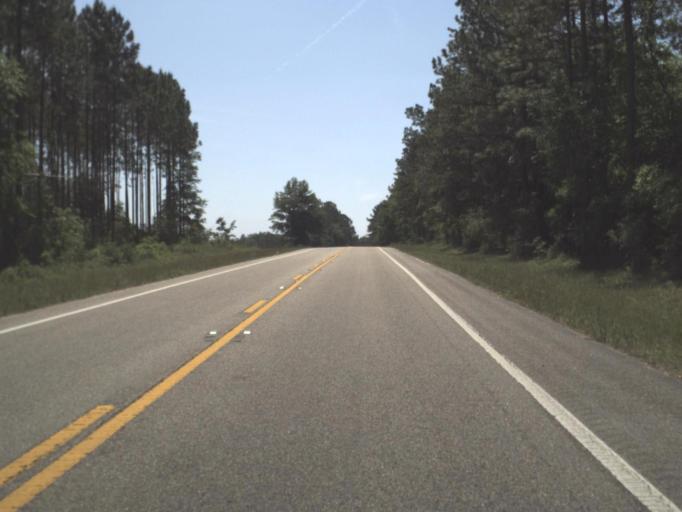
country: US
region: Florida
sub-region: Jackson County
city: Marianna
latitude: 30.6381
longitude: -85.1938
